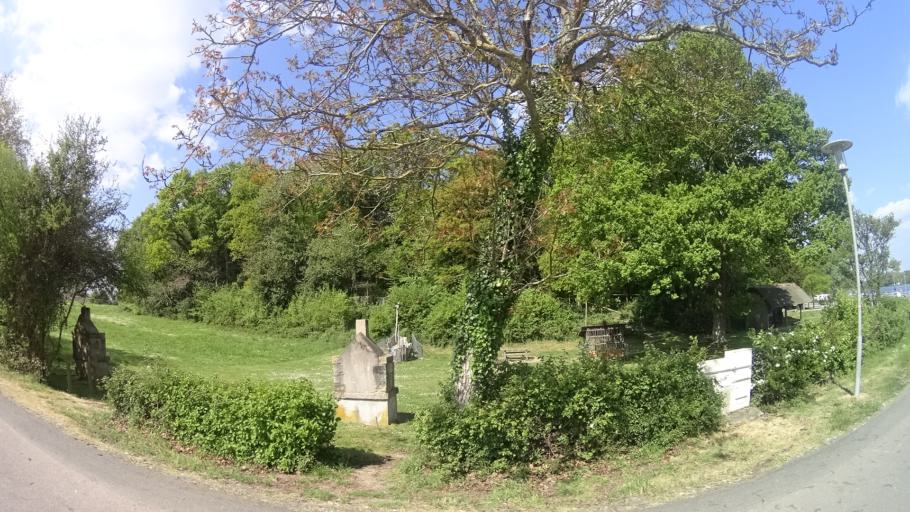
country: FR
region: Brittany
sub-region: Departement du Morbihan
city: Rieux
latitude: 47.5981
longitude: -2.0997
